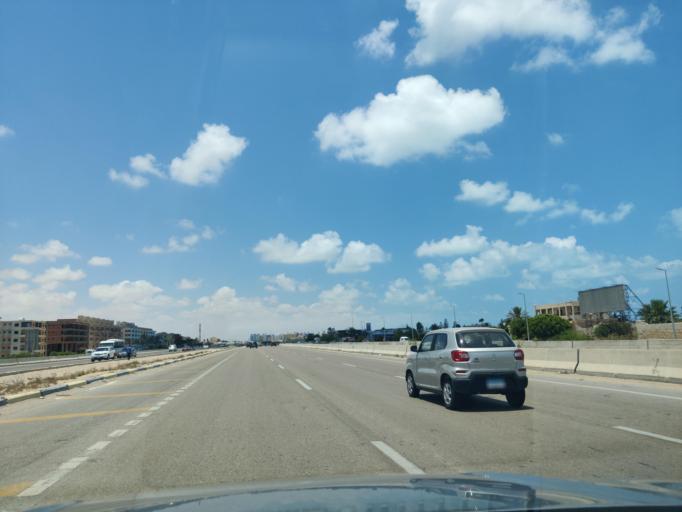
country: EG
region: Muhafazat Matruh
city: Al `Alamayn
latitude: 30.8174
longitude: 29.0299
